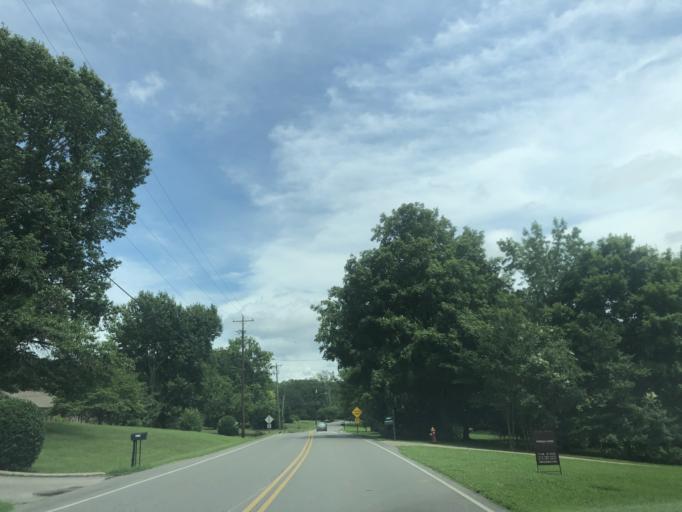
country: US
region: Tennessee
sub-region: Davidson County
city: Forest Hills
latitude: 36.0645
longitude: -86.8184
